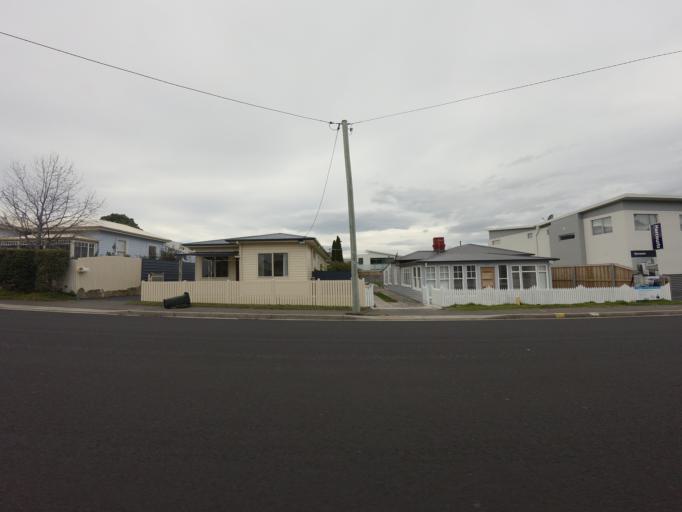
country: AU
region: Tasmania
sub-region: Clarence
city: Bellerive
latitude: -42.8764
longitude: 147.3759
